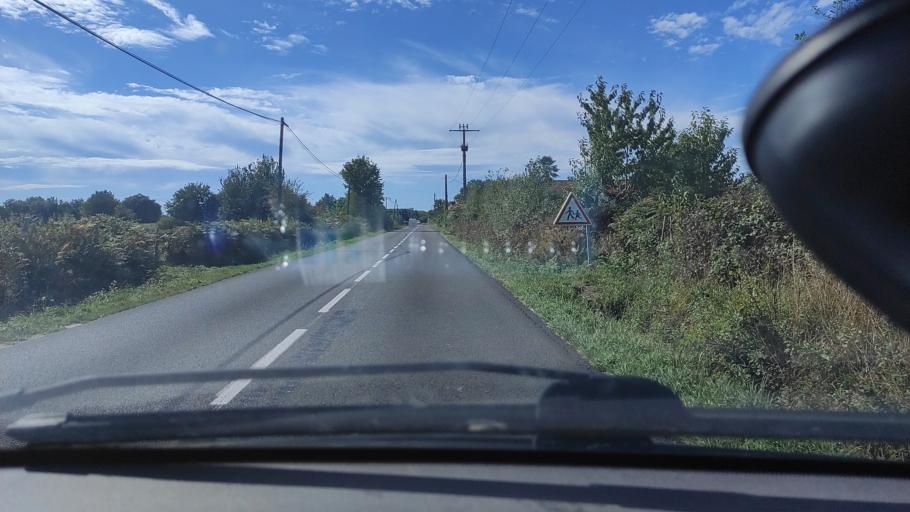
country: FR
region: Pays de la Loire
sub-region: Departement de la Vendee
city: La Boissiere-des-Landes
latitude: 46.5569
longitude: -1.4407
